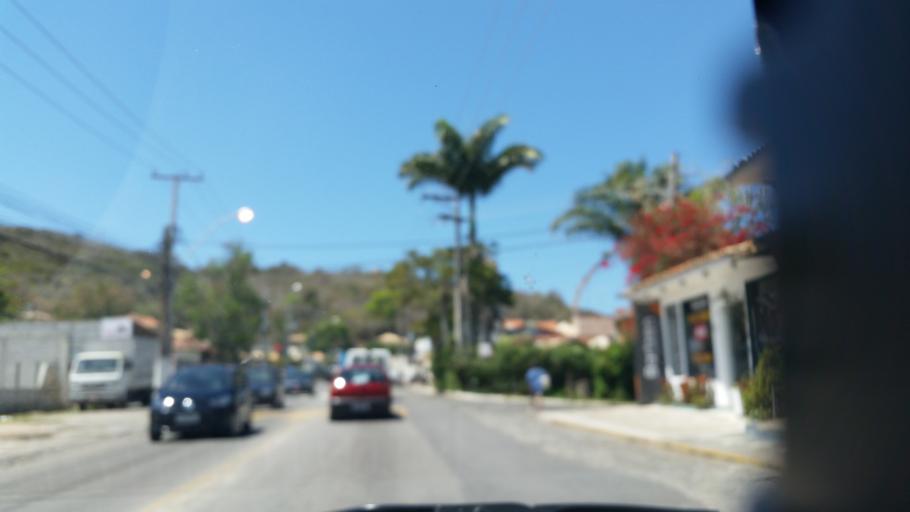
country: BR
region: Rio de Janeiro
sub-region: Armacao De Buzios
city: Armacao de Buzios
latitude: -22.7684
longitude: -41.9077
